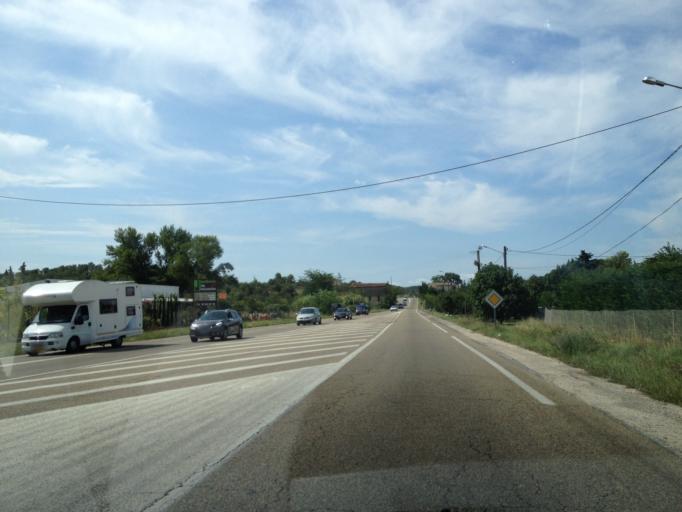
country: FR
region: Languedoc-Roussillon
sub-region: Departement du Gard
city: Rousson
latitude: 44.1884
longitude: 4.1294
